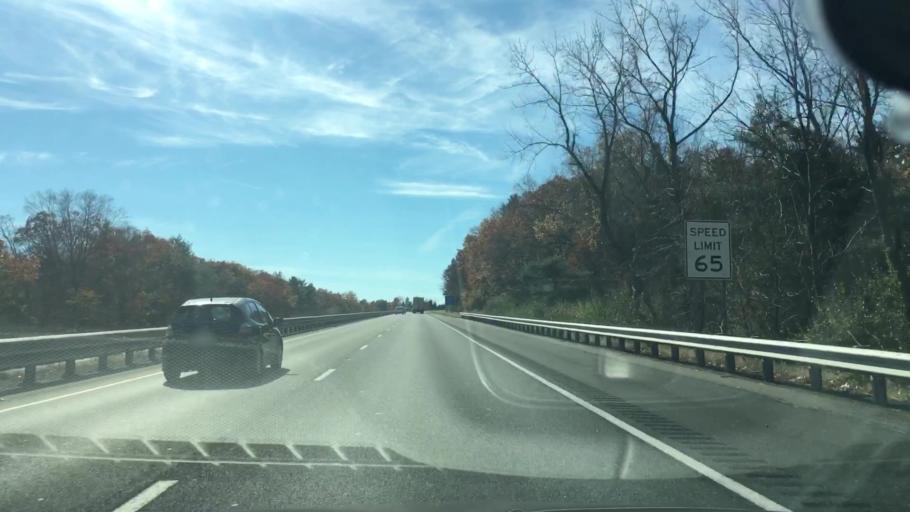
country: US
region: Massachusetts
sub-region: Hampshire County
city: South Hadley
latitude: 42.2627
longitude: -72.6147
